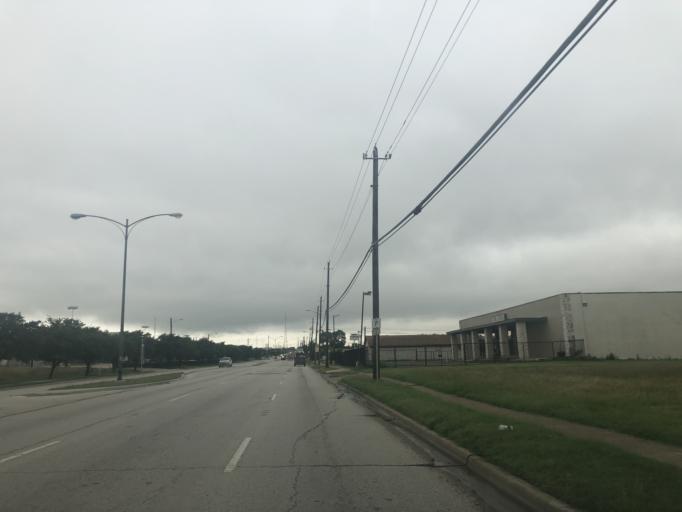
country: US
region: Texas
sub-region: Dallas County
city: Cockrell Hill
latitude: 32.7836
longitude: -96.8739
